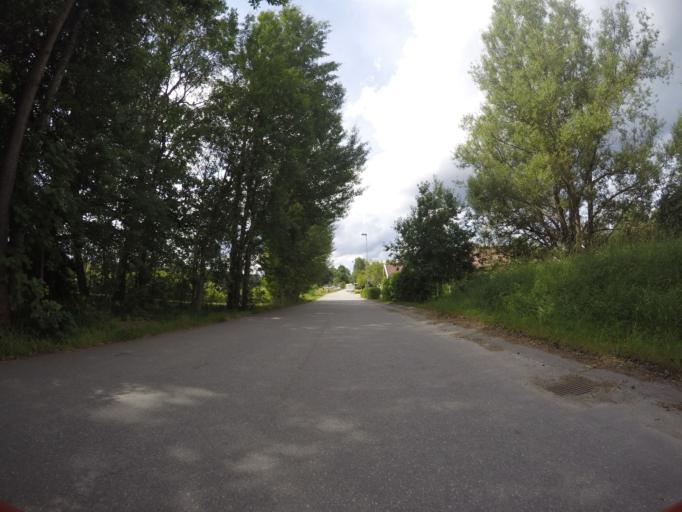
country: SE
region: Vaestra Goetaland
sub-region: Trollhattan
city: Trollhattan
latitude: 58.2285
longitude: 12.3080
